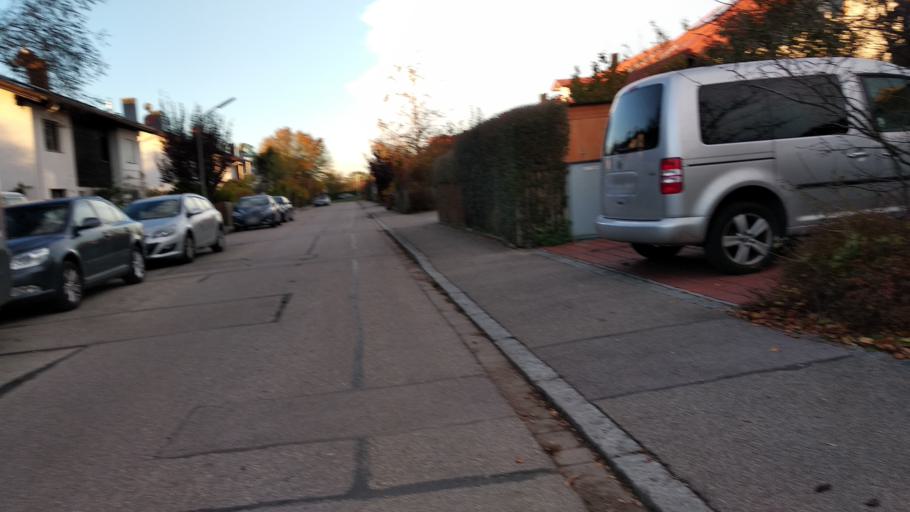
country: DE
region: Bavaria
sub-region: Upper Bavaria
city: Hohenkirchen-Siegertsbrunn
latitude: 48.0241
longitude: 11.7320
